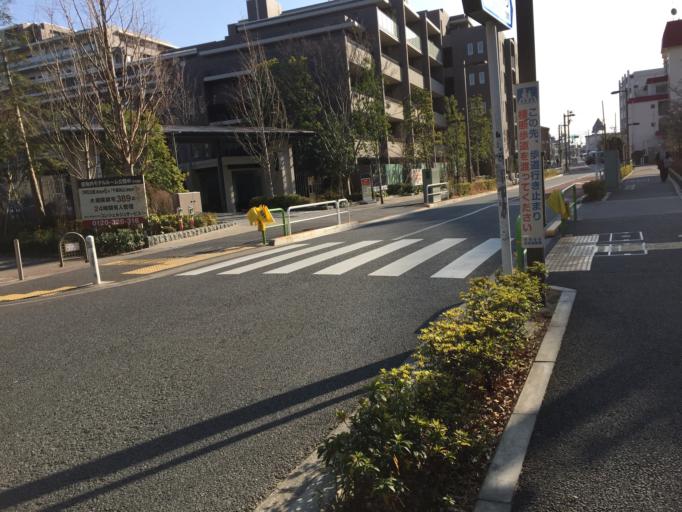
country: JP
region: Tokyo
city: Mitaka-shi
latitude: 35.6670
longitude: 139.6082
